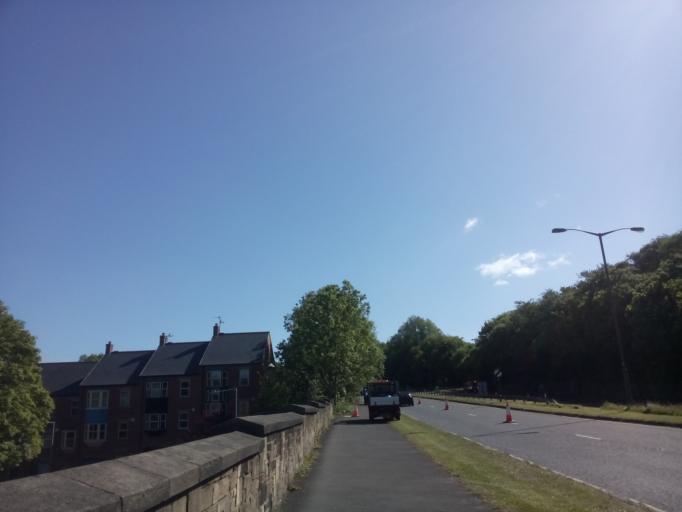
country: GB
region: England
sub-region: County Durham
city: Durham
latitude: 54.7792
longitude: -1.5642
